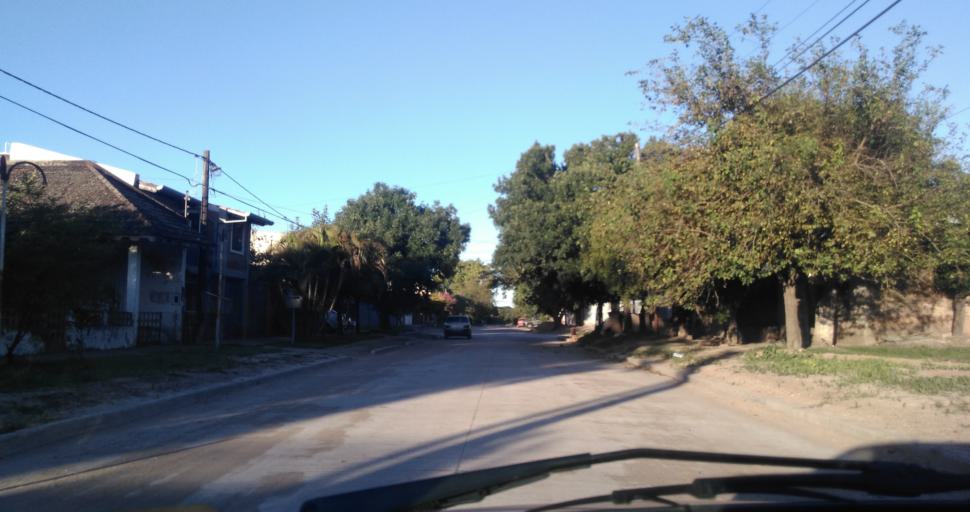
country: AR
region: Chaco
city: Resistencia
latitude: -27.4372
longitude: -58.9728
